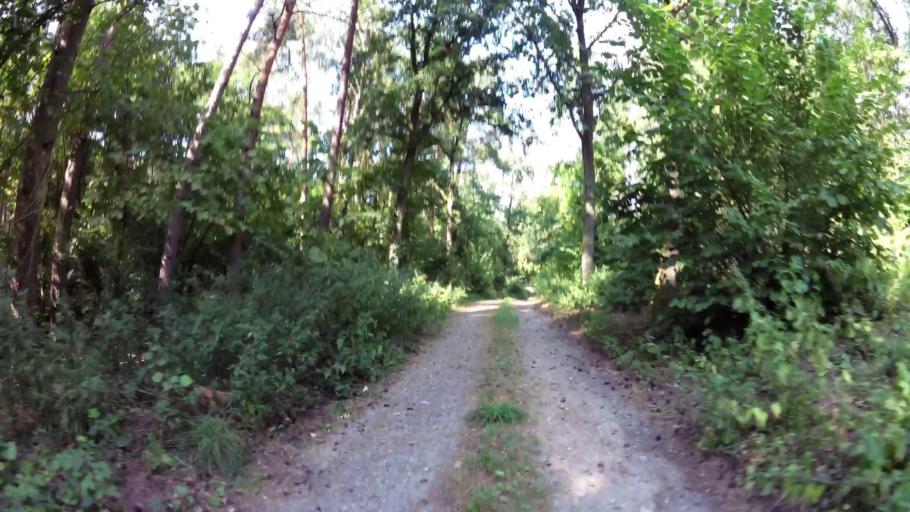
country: PL
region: West Pomeranian Voivodeship
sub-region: Powiat gryfinski
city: Moryn
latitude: 52.8822
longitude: 14.4326
